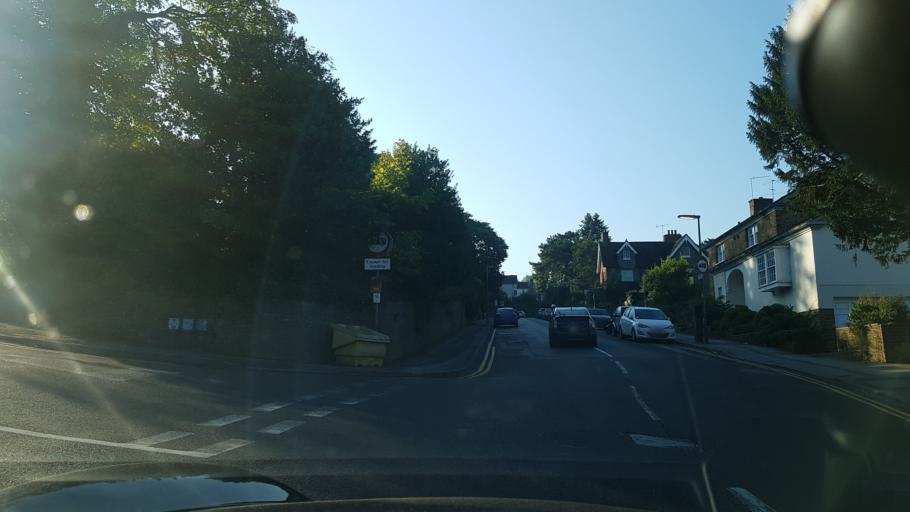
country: GB
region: England
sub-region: Surrey
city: Guildford
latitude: 51.2346
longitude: -0.5712
